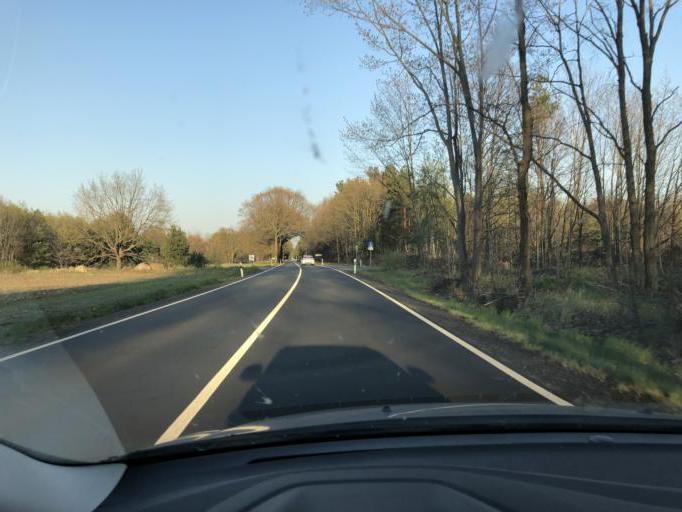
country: DE
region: Saxony
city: Hoyerswerda
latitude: 51.5223
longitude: 14.2486
